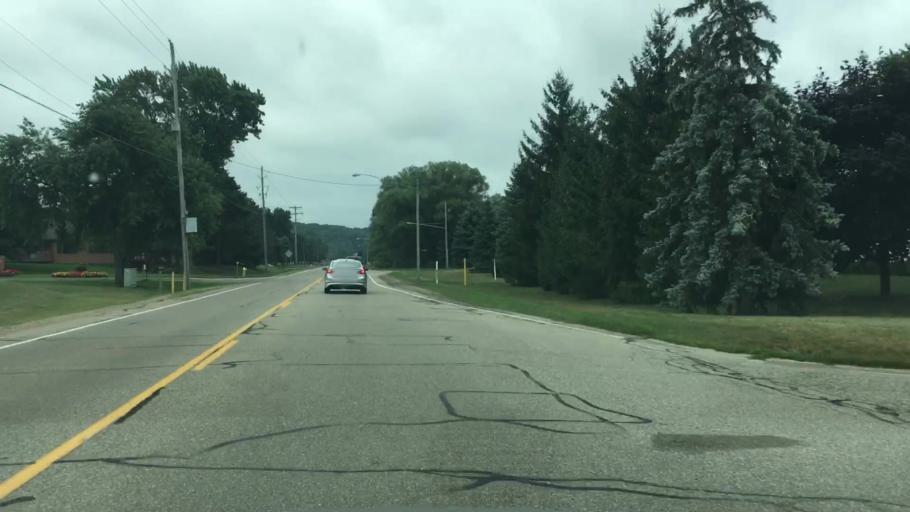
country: US
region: Michigan
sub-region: Ottawa County
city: Jenison
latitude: 42.8822
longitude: -85.8168
